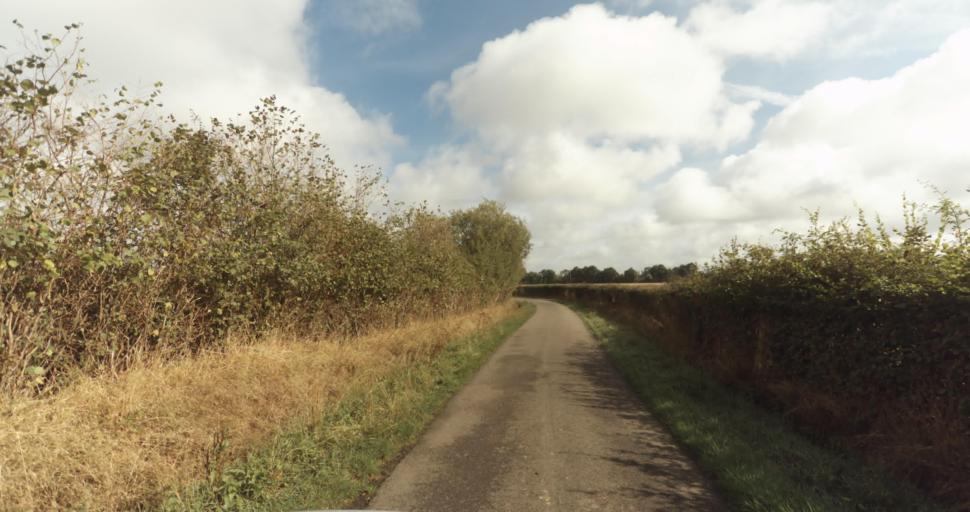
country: FR
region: Lower Normandy
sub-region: Departement de l'Orne
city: Gace
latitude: 48.8445
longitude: 0.3605
